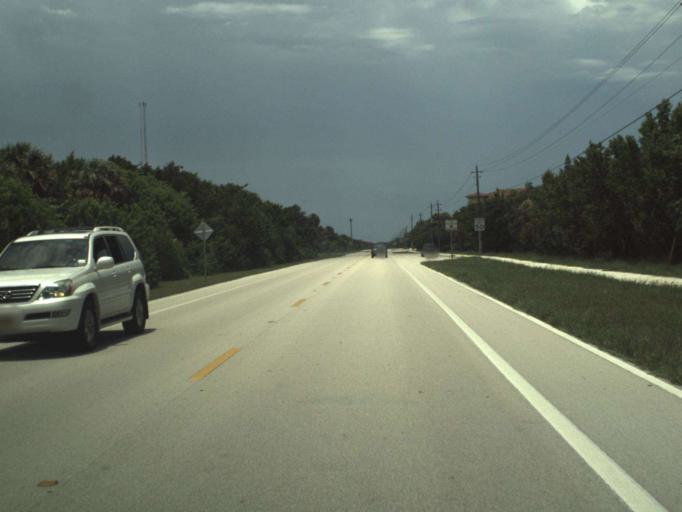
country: US
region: Florida
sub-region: Saint Lucie County
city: Hutchinson Island South
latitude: 27.3260
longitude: -80.2302
